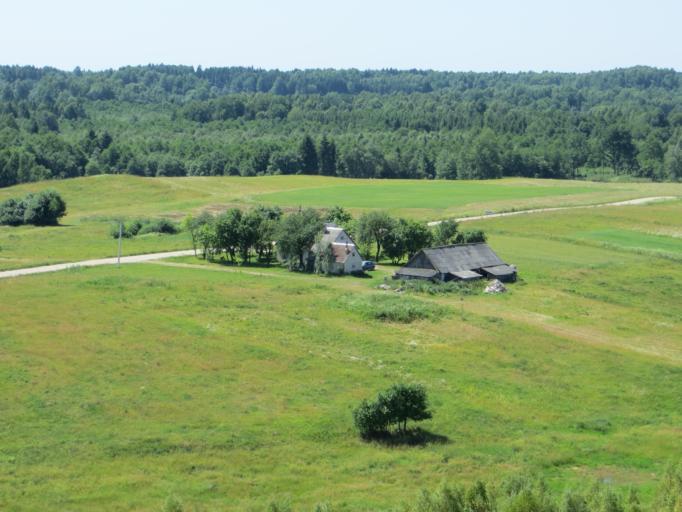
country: LT
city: Aukstadvaris
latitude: 54.6815
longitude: 24.4802
